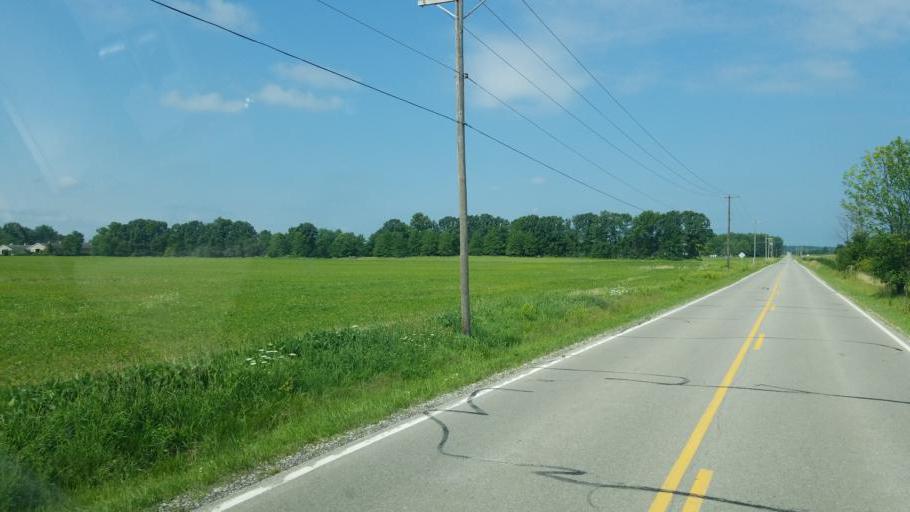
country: US
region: Ohio
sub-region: Crawford County
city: Galion
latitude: 40.7562
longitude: -82.8140
